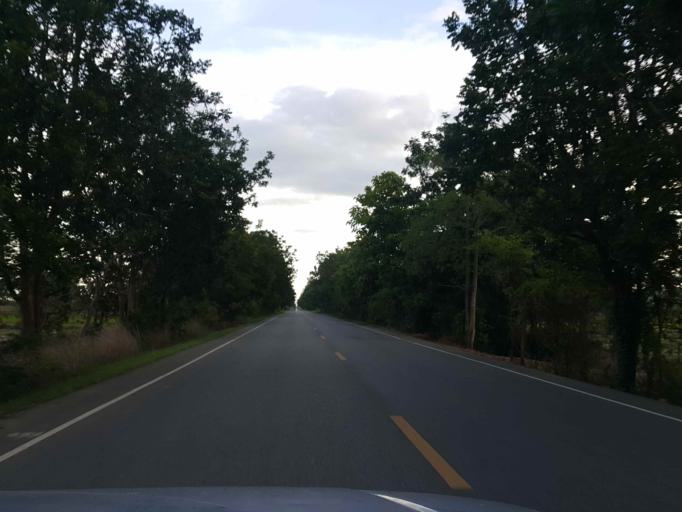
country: TH
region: Sukhothai
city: Sawankhalok
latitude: 17.3174
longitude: 99.7354
